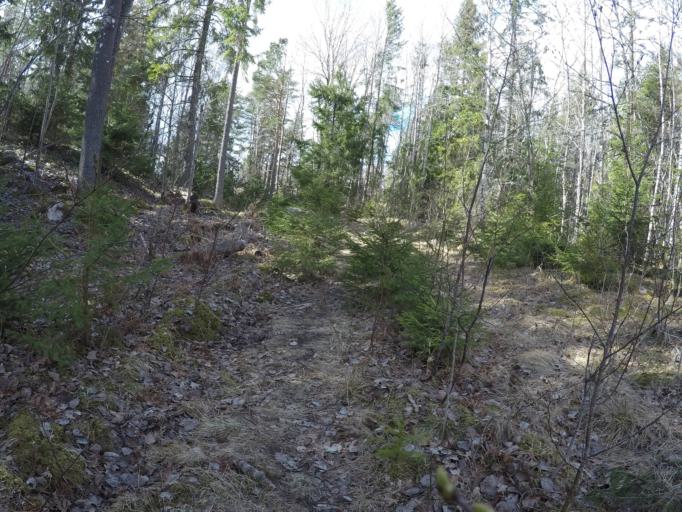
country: SE
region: Soedermanland
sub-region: Eskilstuna Kommun
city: Kvicksund
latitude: 59.4651
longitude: 16.3200
